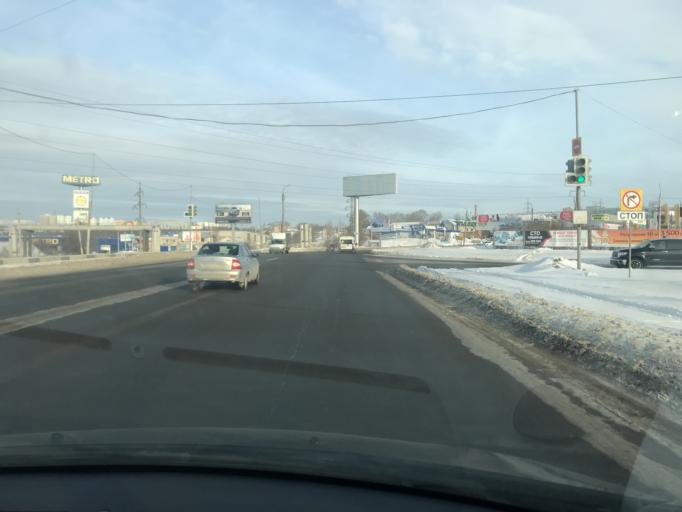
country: RU
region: Ulyanovsk
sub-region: Ulyanovskiy Rayon
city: Ulyanovsk
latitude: 54.3267
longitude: 48.3574
